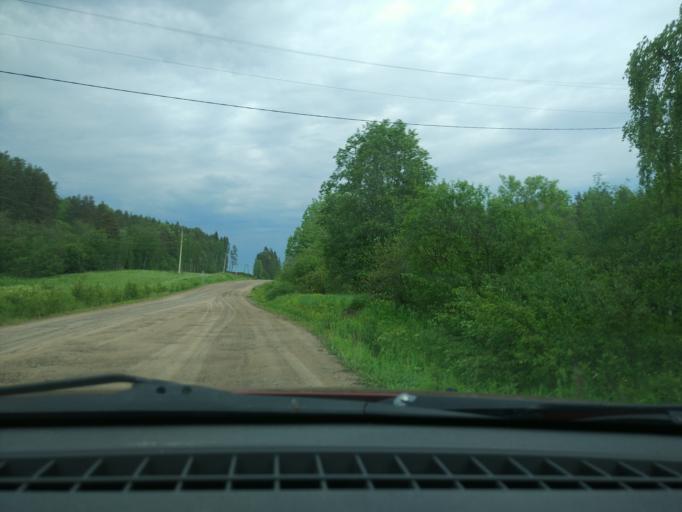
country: RU
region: Leningrad
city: Kuznechnoye
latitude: 61.2713
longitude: 29.8364
